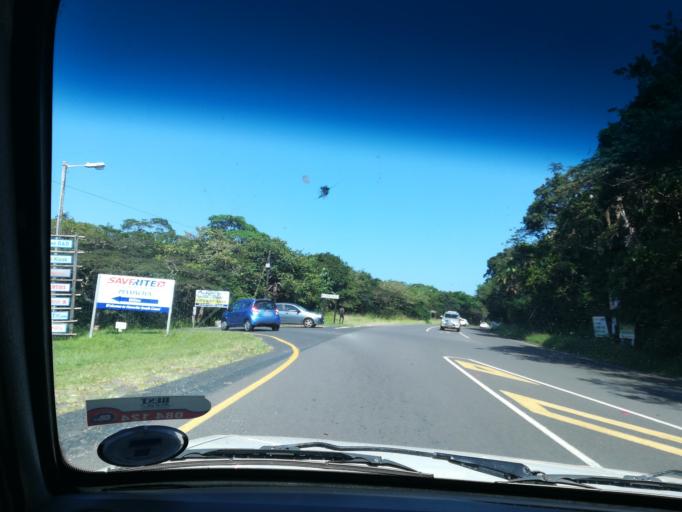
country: ZA
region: KwaZulu-Natal
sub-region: Ugu District Municipality
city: Scottburgh
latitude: -30.3796
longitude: 30.6899
